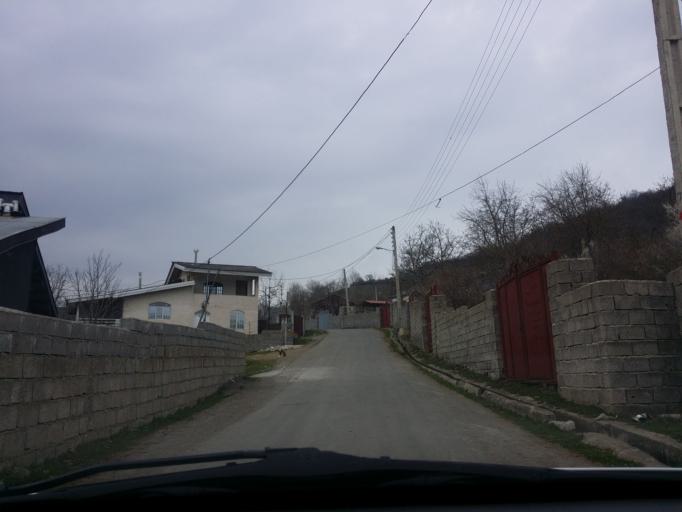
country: IR
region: Mazandaran
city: `Abbasabad
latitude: 36.5496
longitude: 51.1689
